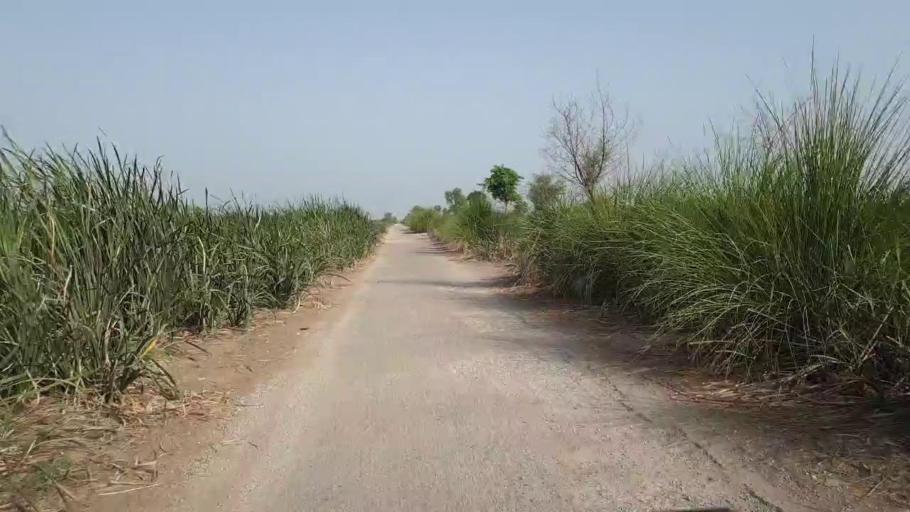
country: PK
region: Sindh
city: Daur
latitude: 26.3438
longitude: 68.1794
